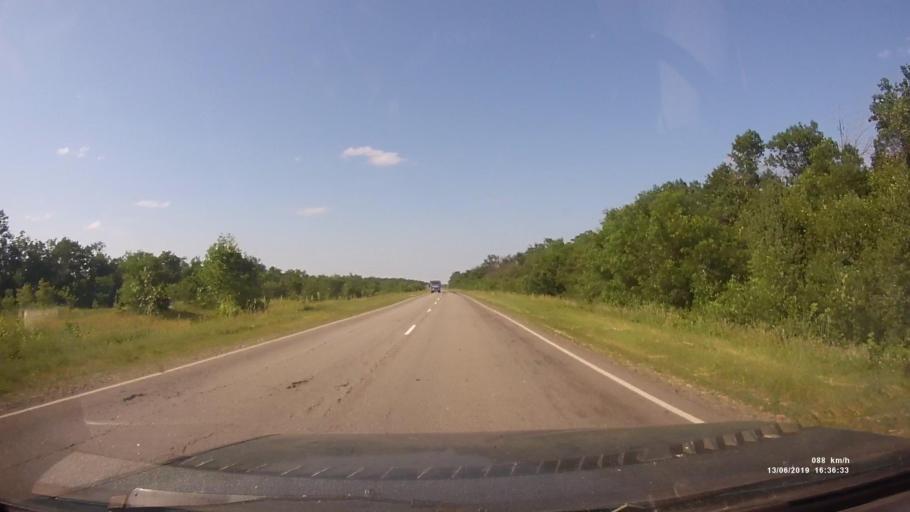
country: RU
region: Rostov
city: Kazanskaya
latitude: 49.8965
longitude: 41.3067
